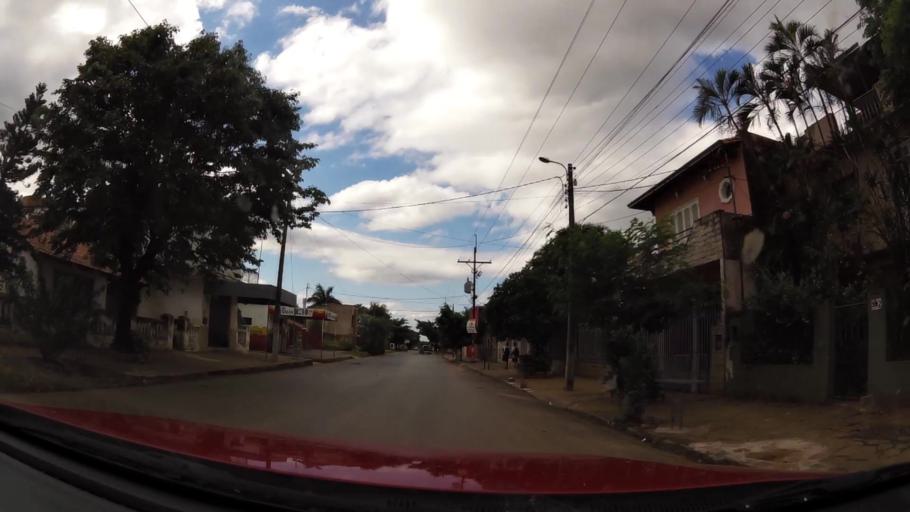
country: PY
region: Central
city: San Lorenzo
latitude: -25.2705
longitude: -57.5025
